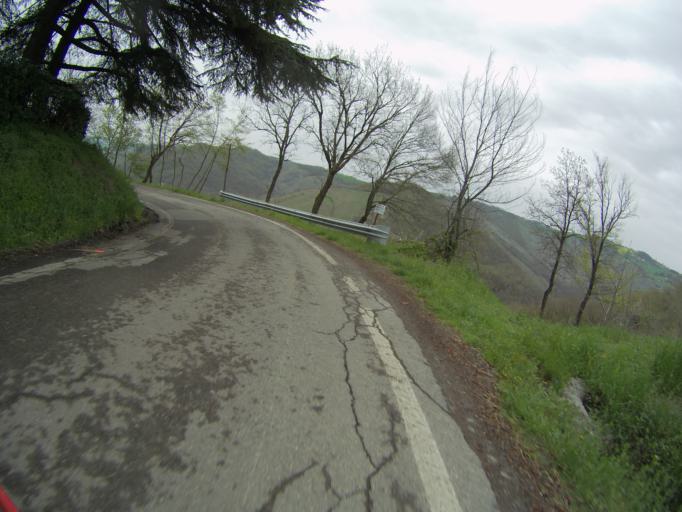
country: IT
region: Emilia-Romagna
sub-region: Provincia di Reggio Emilia
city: San Polo d'Enza
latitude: 44.6074
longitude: 10.4474
